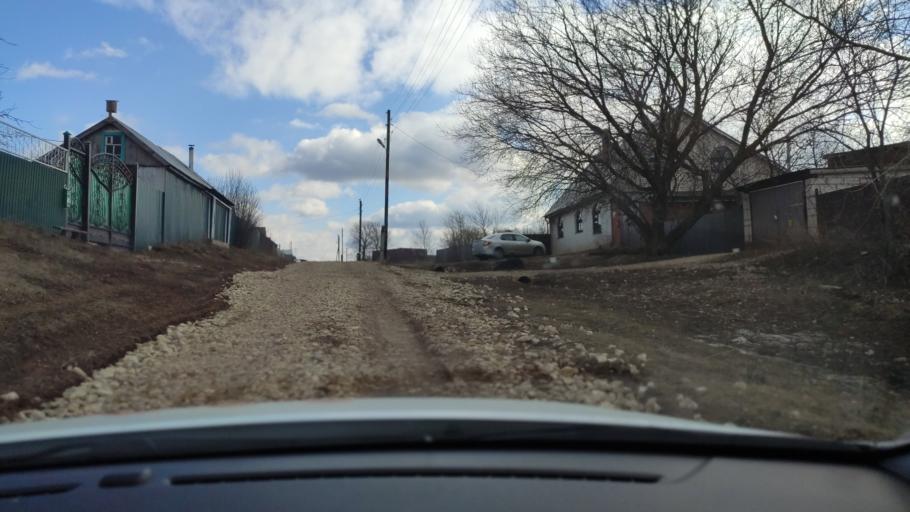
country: RU
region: Tatarstan
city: Vysokaya Gora
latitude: 56.2083
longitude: 49.3158
